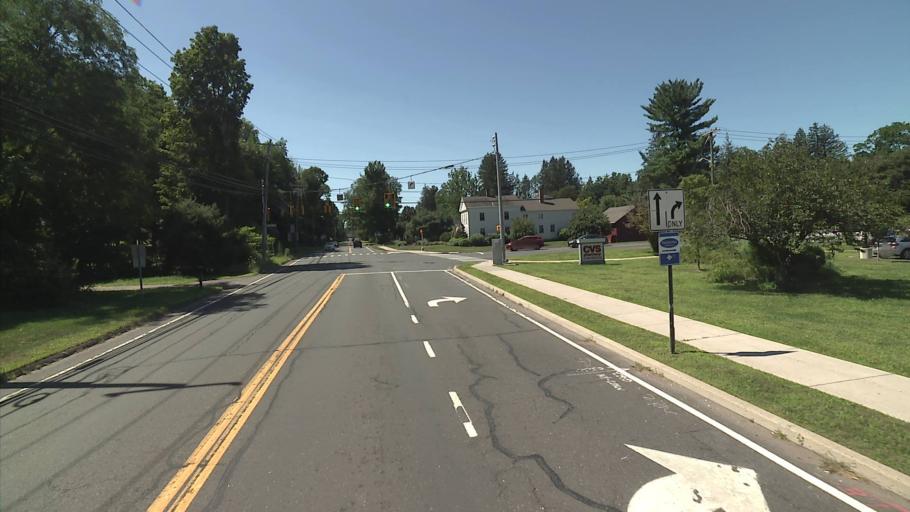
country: US
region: Connecticut
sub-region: Hartford County
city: Farmington
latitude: 41.7043
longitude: -72.8432
